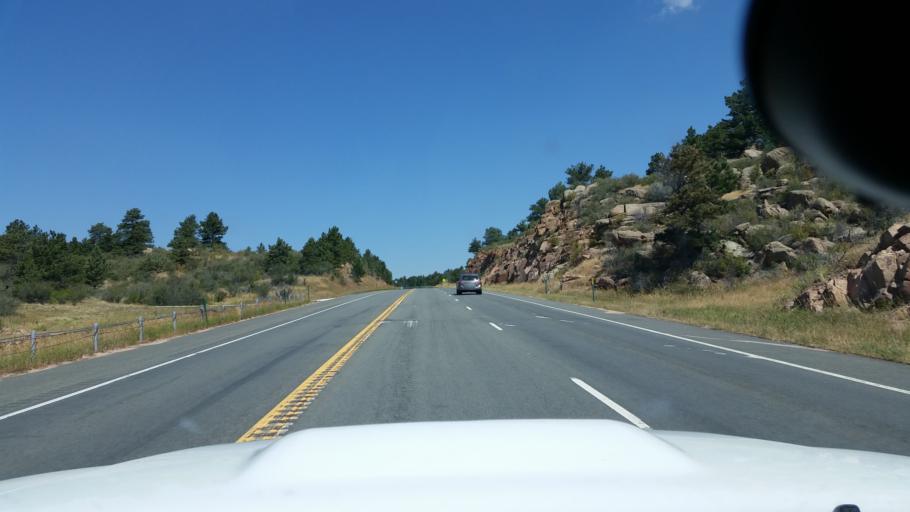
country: US
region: Wyoming
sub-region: Albany County
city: Laramie
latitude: 40.9705
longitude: -105.3815
